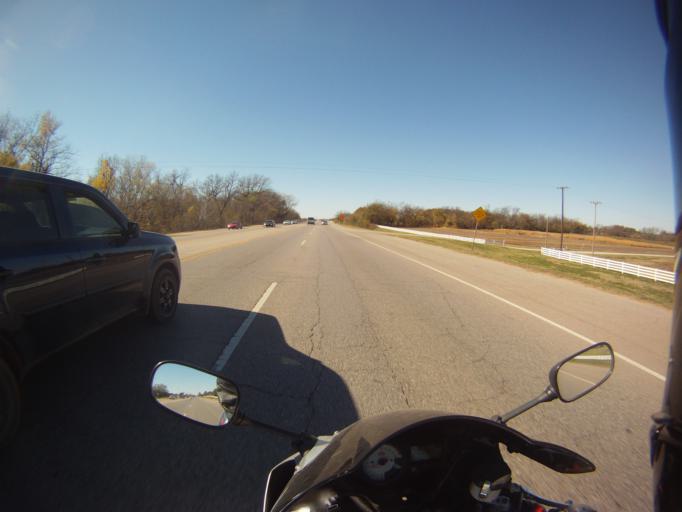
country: US
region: Oklahoma
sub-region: Payne County
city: Stillwater
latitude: 36.1158
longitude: -97.0955
